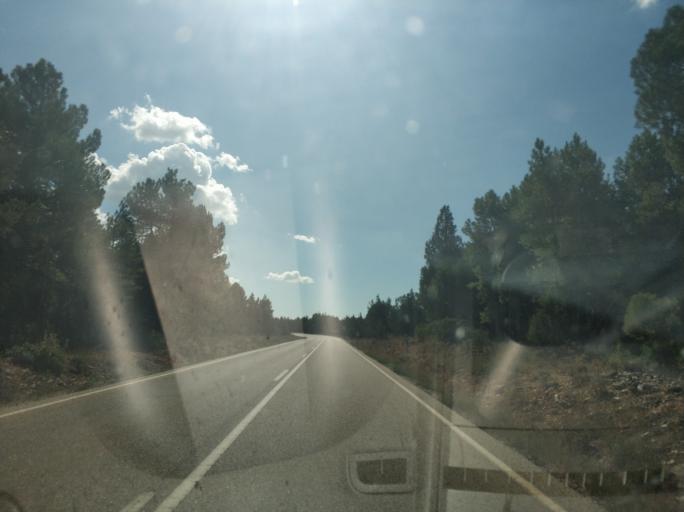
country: ES
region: Castille and Leon
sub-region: Provincia de Soria
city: Ucero
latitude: 41.7405
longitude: -3.0448
